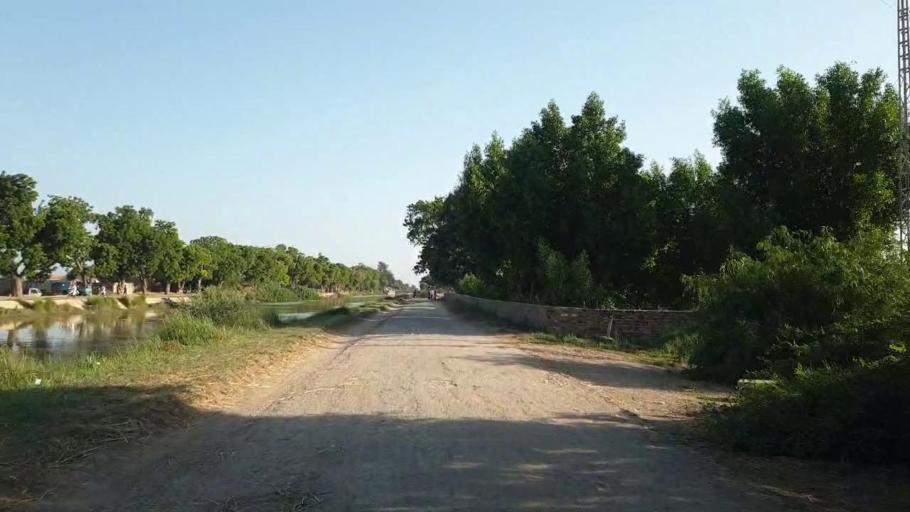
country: PK
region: Sindh
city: Hyderabad
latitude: 25.3200
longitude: 68.4280
